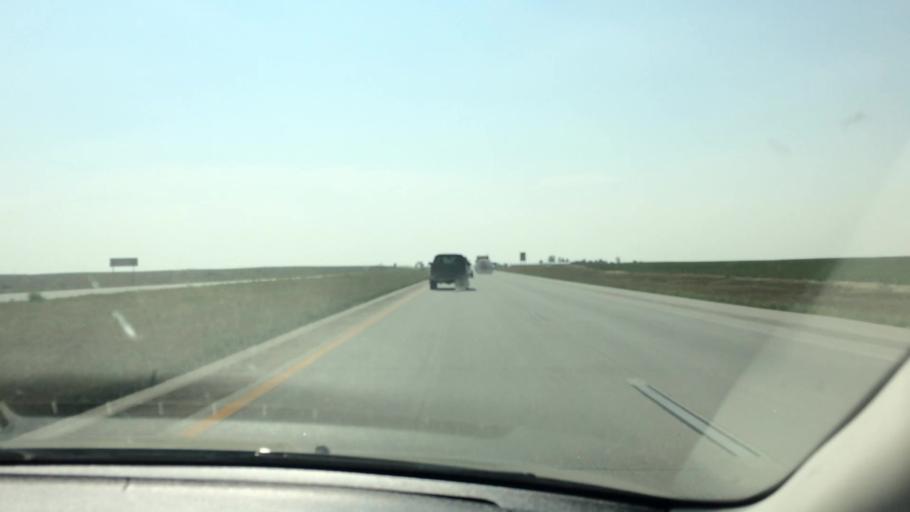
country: US
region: Colorado
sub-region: Adams County
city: Bennett
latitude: 39.7387
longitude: -104.5082
